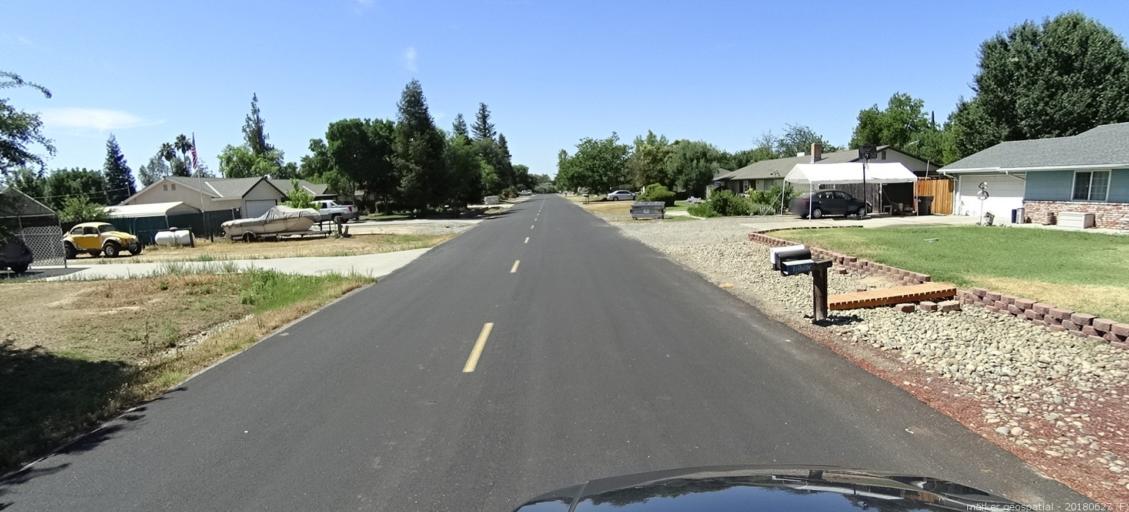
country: US
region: California
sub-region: Madera County
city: Bonadelle Ranchos-Madera Ranchos
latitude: 36.9277
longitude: -119.8795
